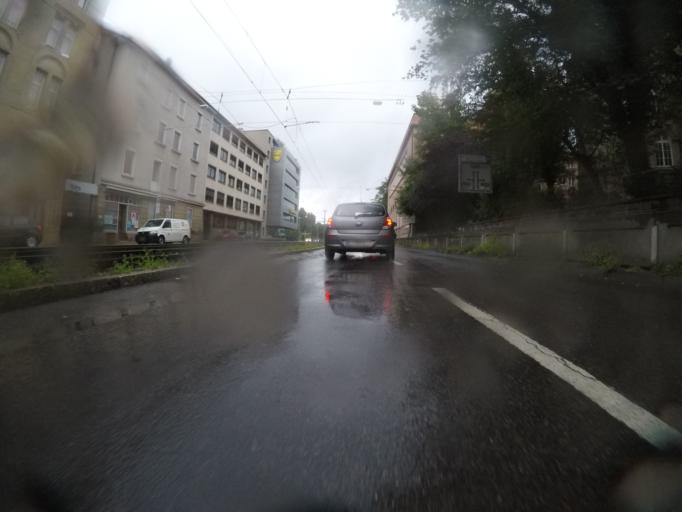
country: DE
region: Baden-Wuerttemberg
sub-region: Regierungsbezirk Stuttgart
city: Stuttgart
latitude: 48.7763
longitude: 9.1659
